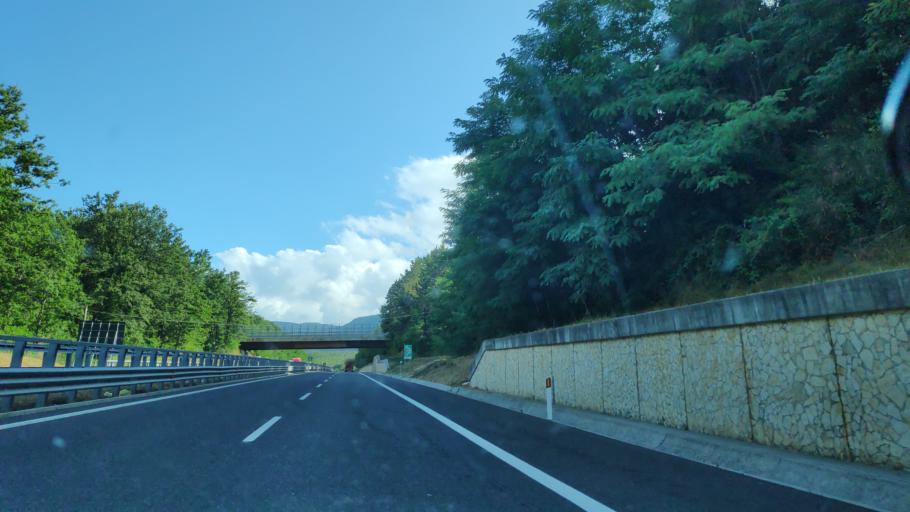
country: IT
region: Campania
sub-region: Provincia di Salerno
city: Casalbuono
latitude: 40.2472
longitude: 15.6598
